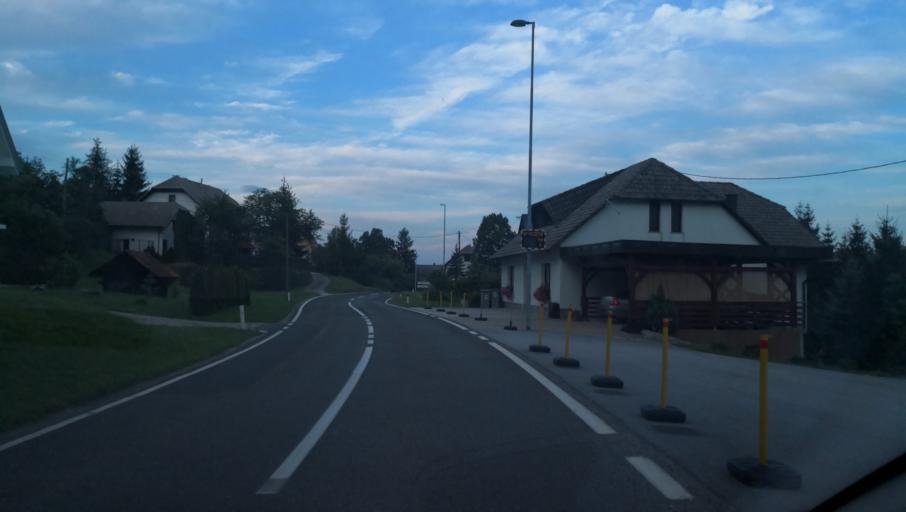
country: SI
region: Metlika
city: Metlika
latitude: 45.6945
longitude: 15.2595
